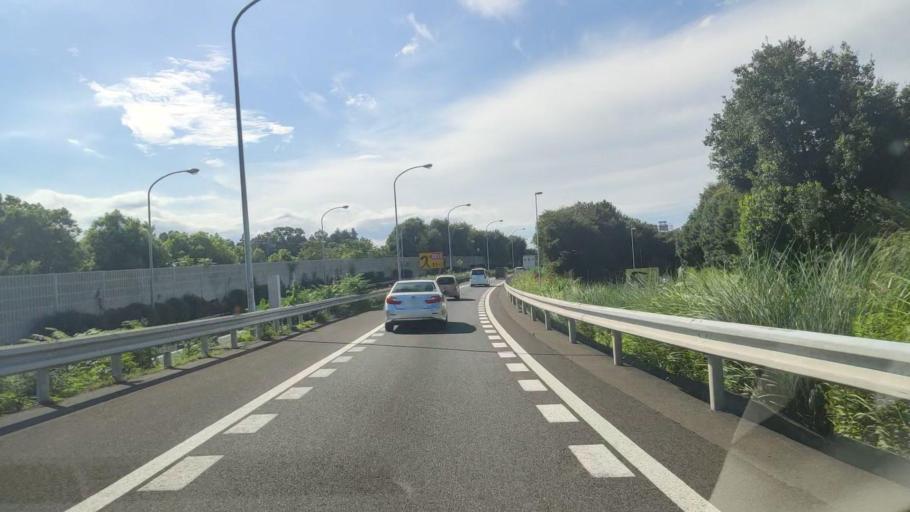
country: JP
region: Saitama
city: Sakado
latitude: 35.9315
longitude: 139.4053
